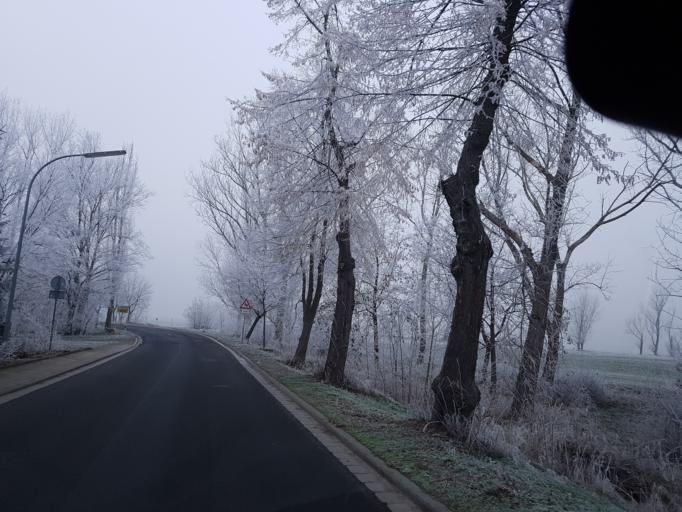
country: DE
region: Brandenburg
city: Muhlberg
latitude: 51.4232
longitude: 13.2620
